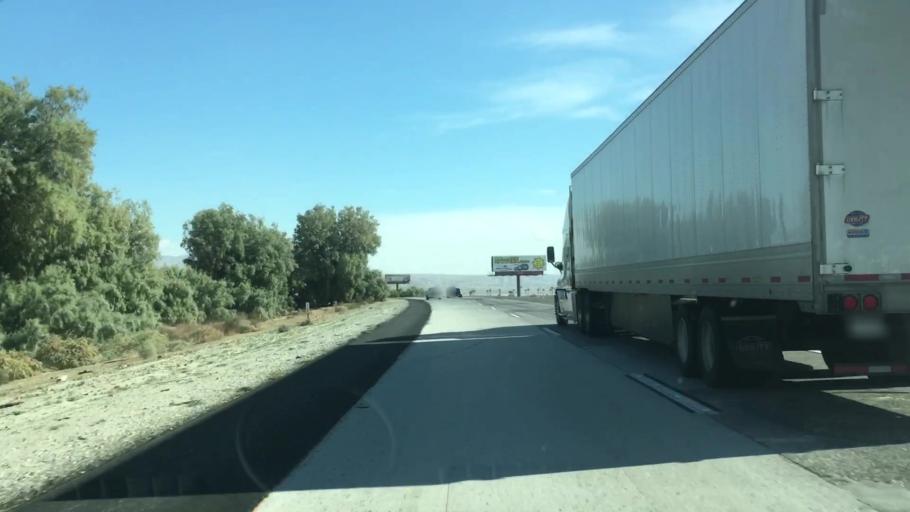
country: US
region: California
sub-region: Riverside County
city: Indio
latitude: 33.7154
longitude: -116.1879
